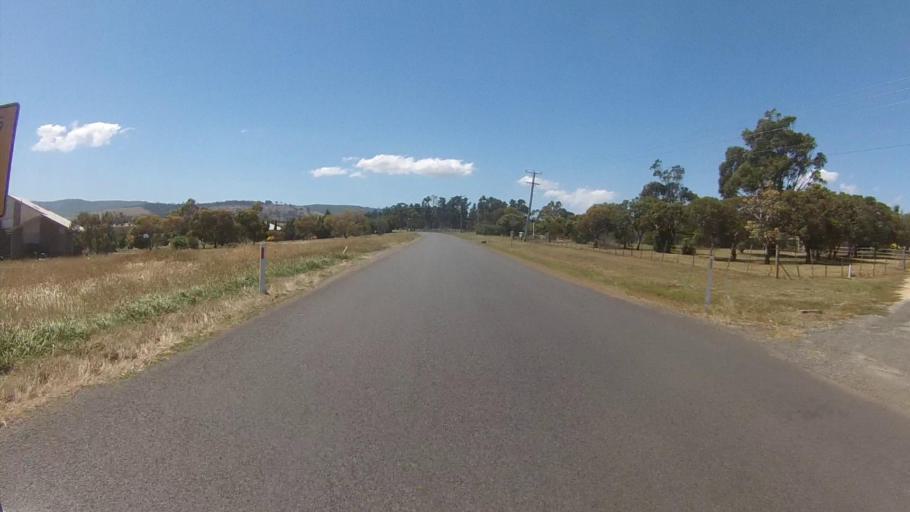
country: AU
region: Tasmania
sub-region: Sorell
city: Sorell
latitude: -42.7809
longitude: 147.5769
